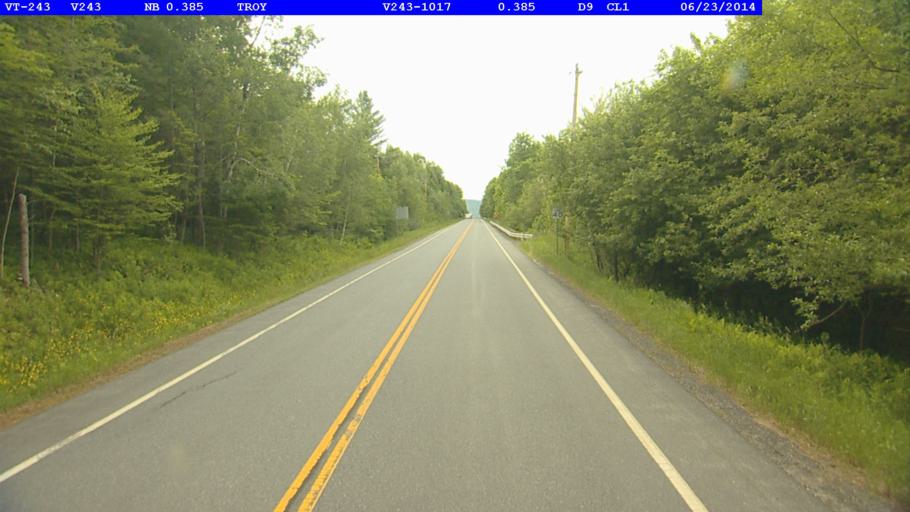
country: US
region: Vermont
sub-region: Orleans County
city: Newport
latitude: 45.0020
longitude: -72.4128
